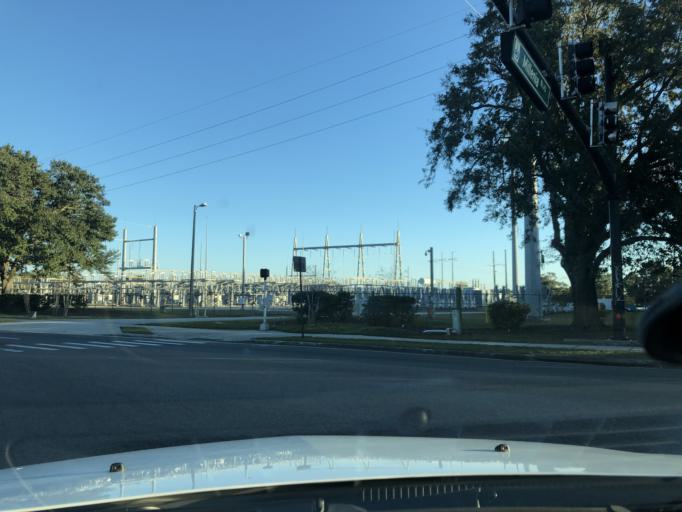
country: US
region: Florida
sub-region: Orange County
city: Tangelo Park
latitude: 28.4721
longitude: -81.4422
